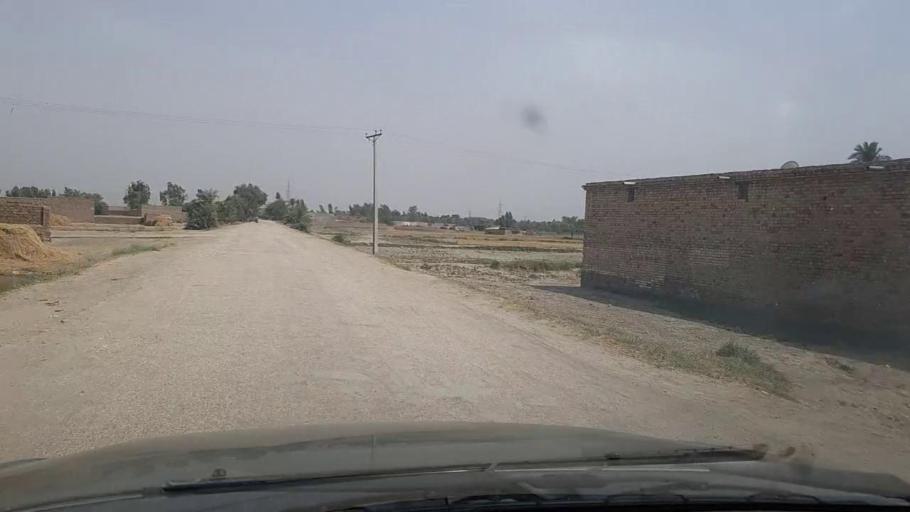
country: PK
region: Sindh
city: Shikarpur
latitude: 27.9269
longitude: 68.6654
